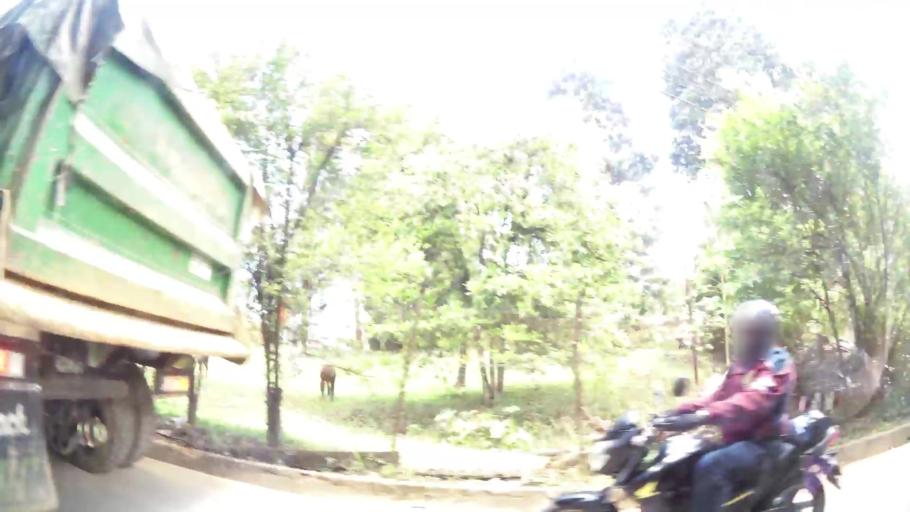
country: CO
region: Antioquia
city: La Estrella
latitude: 6.1644
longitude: -75.6395
